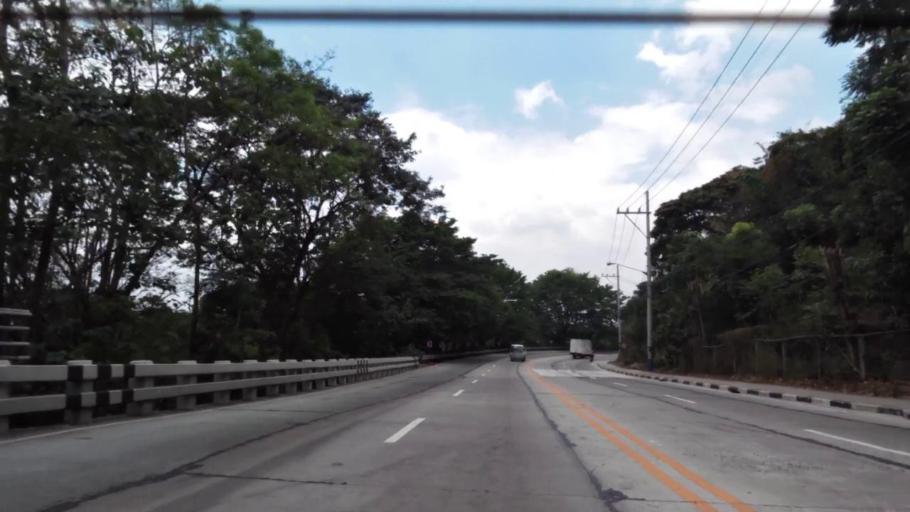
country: PH
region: Calabarzon
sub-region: Province of Rizal
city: Antipolo
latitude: 14.6142
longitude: 121.1516
